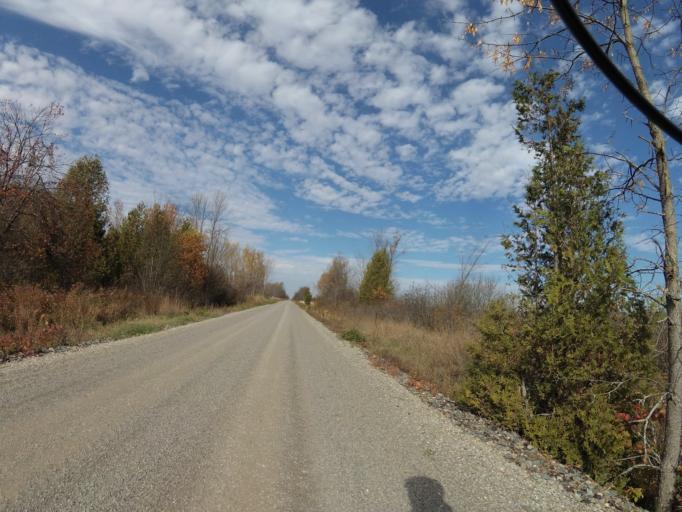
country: CA
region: Ontario
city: Carleton Place
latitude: 45.0374
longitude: -76.0830
